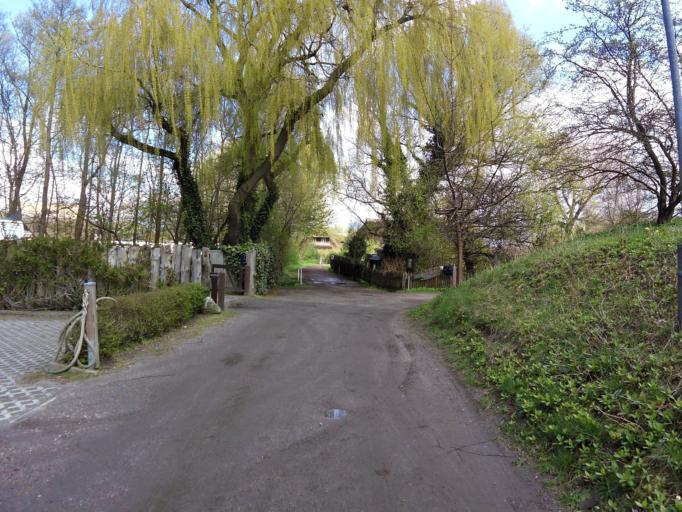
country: DE
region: Mecklenburg-Vorpommern
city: Saal
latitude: 54.3782
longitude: 12.4196
